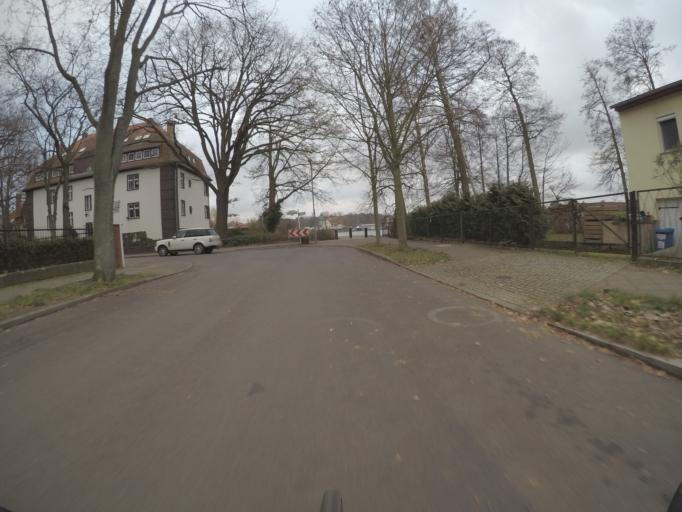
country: DE
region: Berlin
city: Grunau
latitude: 52.4142
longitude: 13.5904
